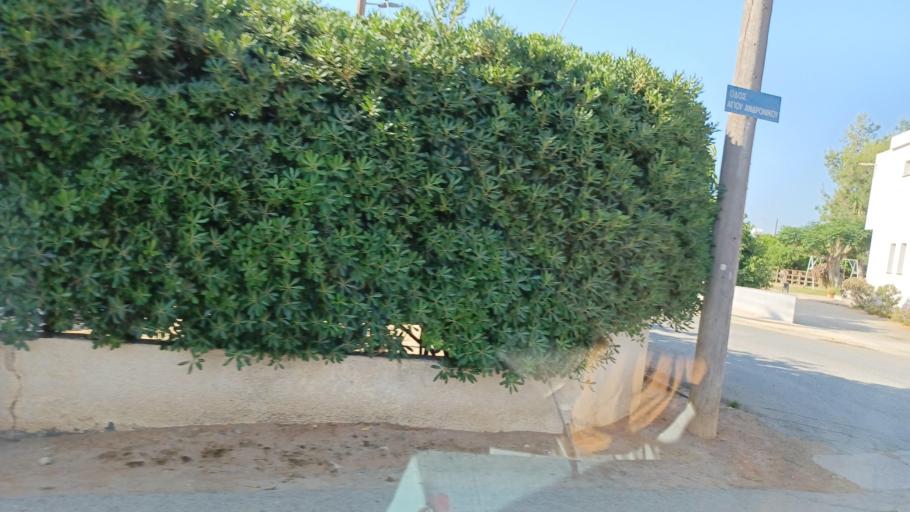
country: CY
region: Ammochostos
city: Frenaros
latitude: 35.0407
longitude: 33.9279
